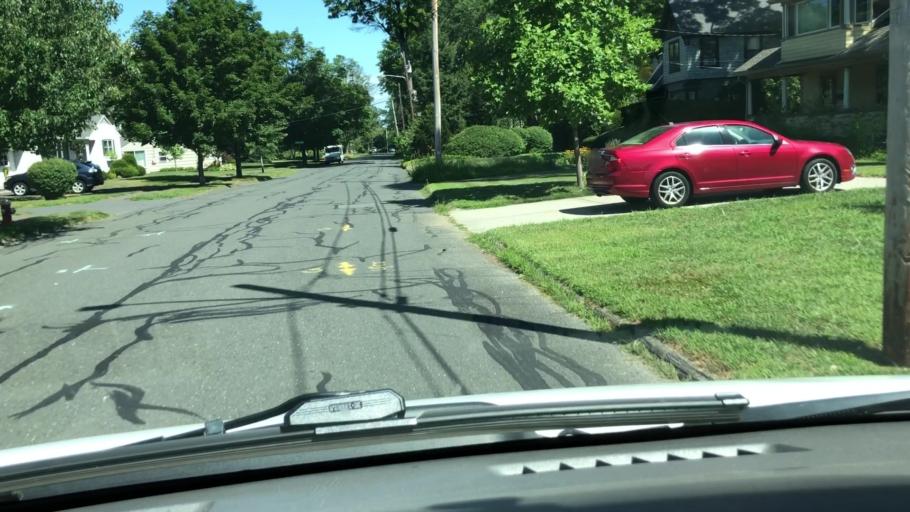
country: US
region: Massachusetts
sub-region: Hampshire County
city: Northampton
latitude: 42.3322
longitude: -72.6681
